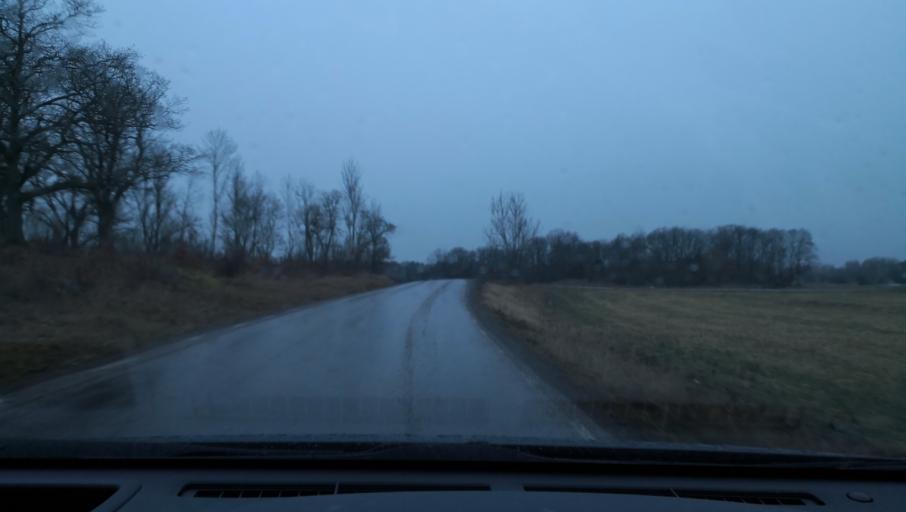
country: SE
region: Soedermanland
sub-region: Eskilstuna Kommun
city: Arla
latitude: 59.4204
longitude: 16.7084
